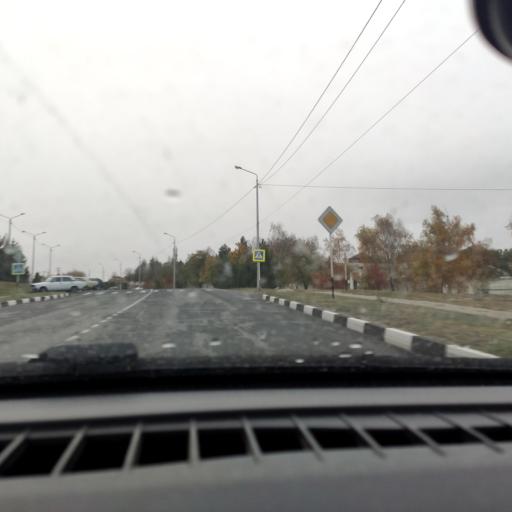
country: RU
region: Belgorod
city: Alekseyevka
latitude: 50.6427
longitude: 38.6905
